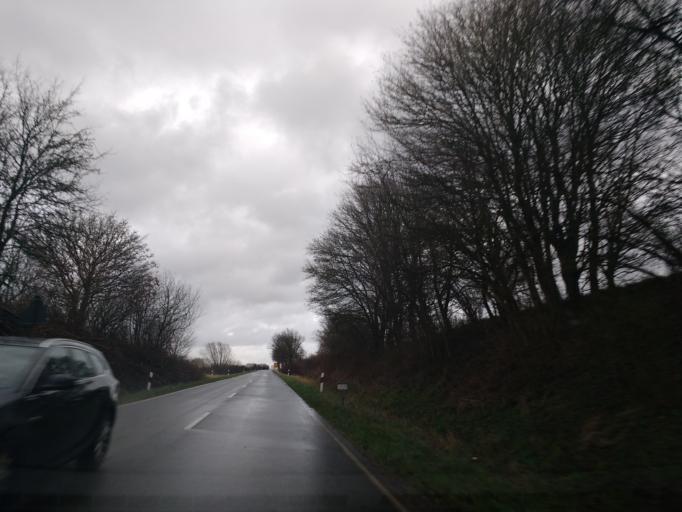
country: DE
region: Schleswig-Holstein
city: Blekendorf
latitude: 54.2968
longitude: 10.6713
